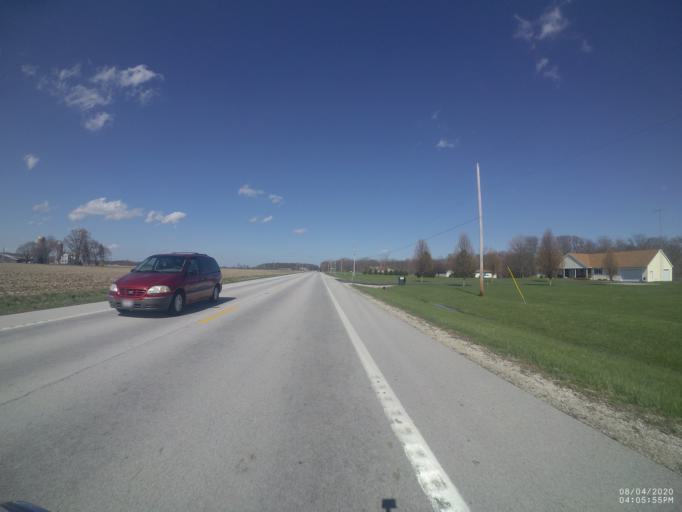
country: US
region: Ohio
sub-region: Sandusky County
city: Ballville
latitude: 41.2665
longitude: -83.2080
